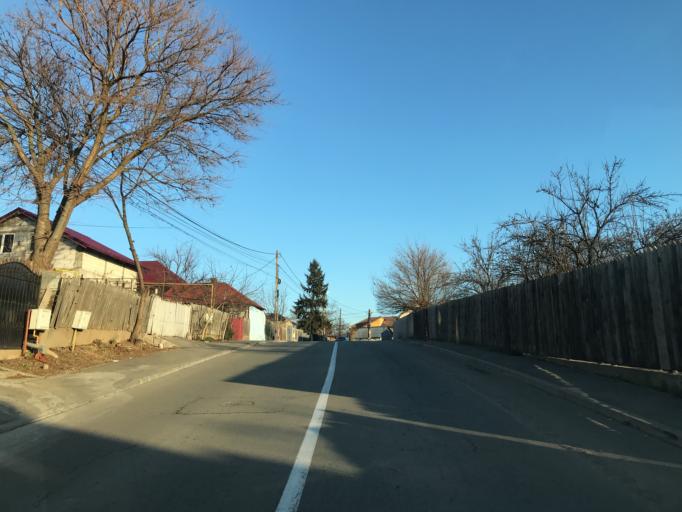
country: RO
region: Olt
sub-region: Municipiul Slatina
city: Slatina
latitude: 44.4172
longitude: 24.3706
